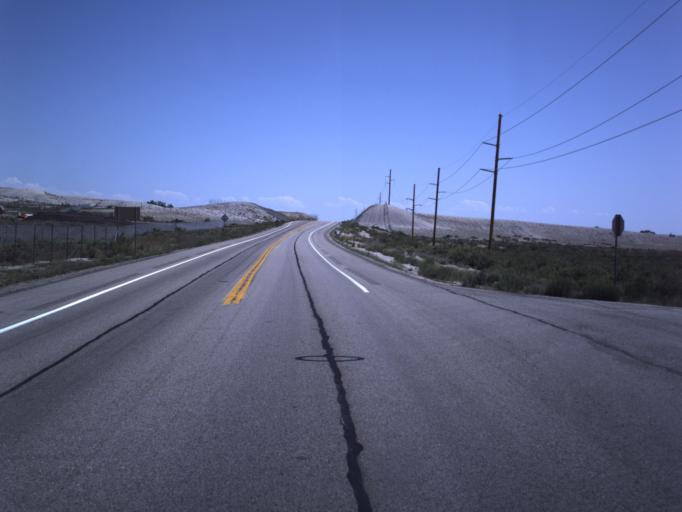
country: US
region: Utah
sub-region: Emery County
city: Ferron
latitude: 38.9245
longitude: -111.2410
